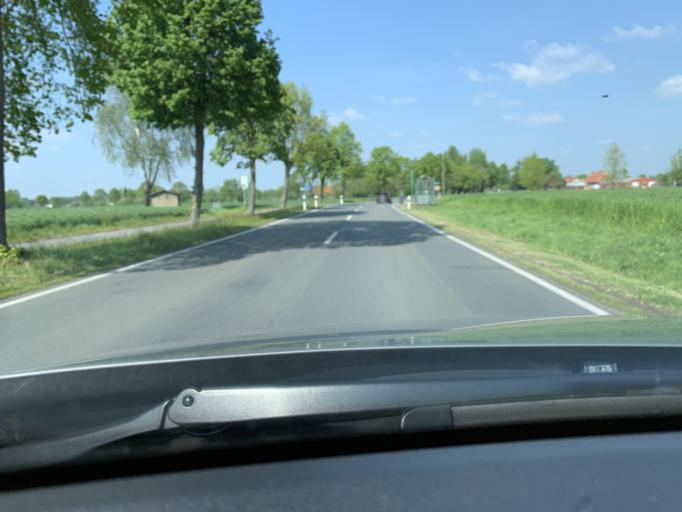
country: DE
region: North Rhine-Westphalia
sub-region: Regierungsbezirk Detmold
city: Langenberg
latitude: 51.7862
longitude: 8.3686
